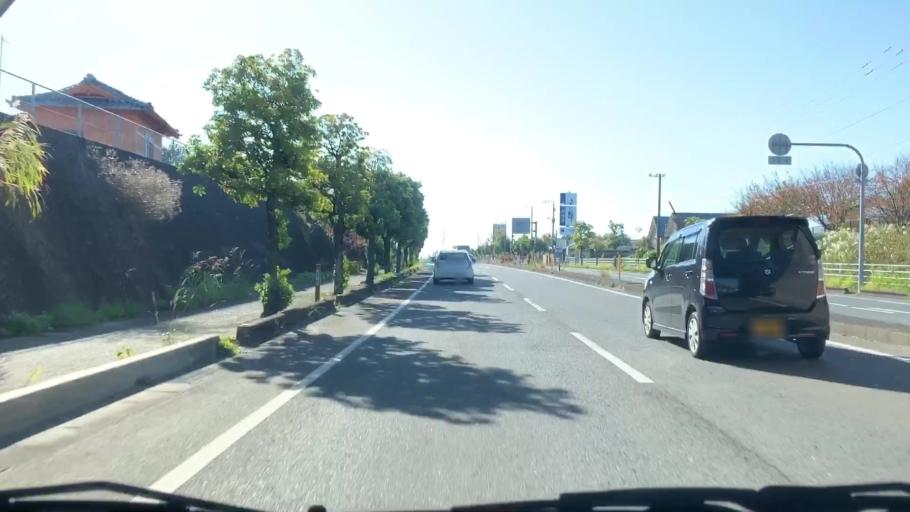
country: JP
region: Saga Prefecture
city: Saga-shi
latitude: 33.3092
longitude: 130.2767
